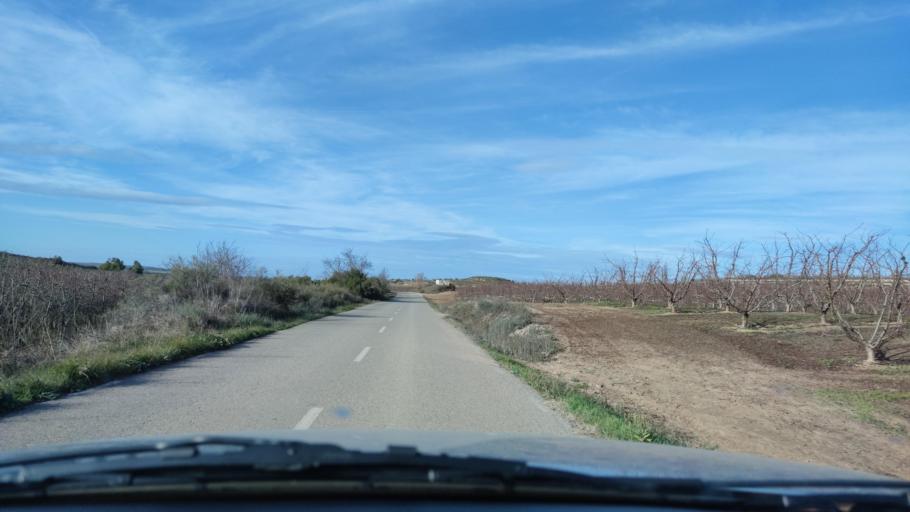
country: ES
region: Catalonia
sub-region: Provincia de Lleida
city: el Cogul
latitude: 41.4691
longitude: 0.6621
